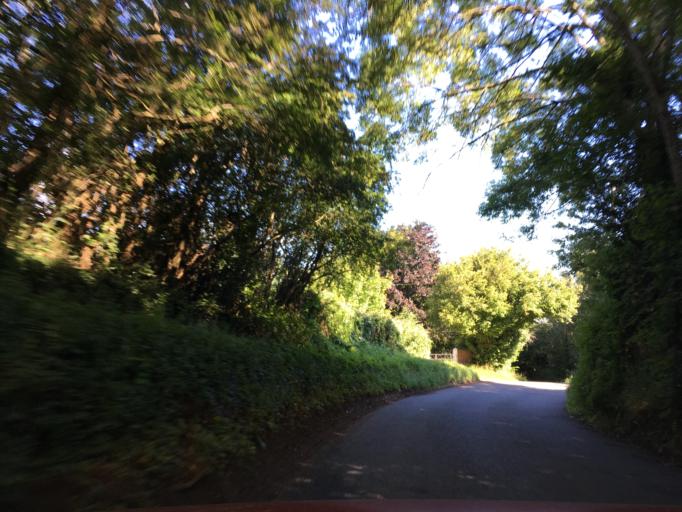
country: GB
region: England
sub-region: Herefordshire
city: Ross on Wye
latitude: 51.9264
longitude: -2.5828
